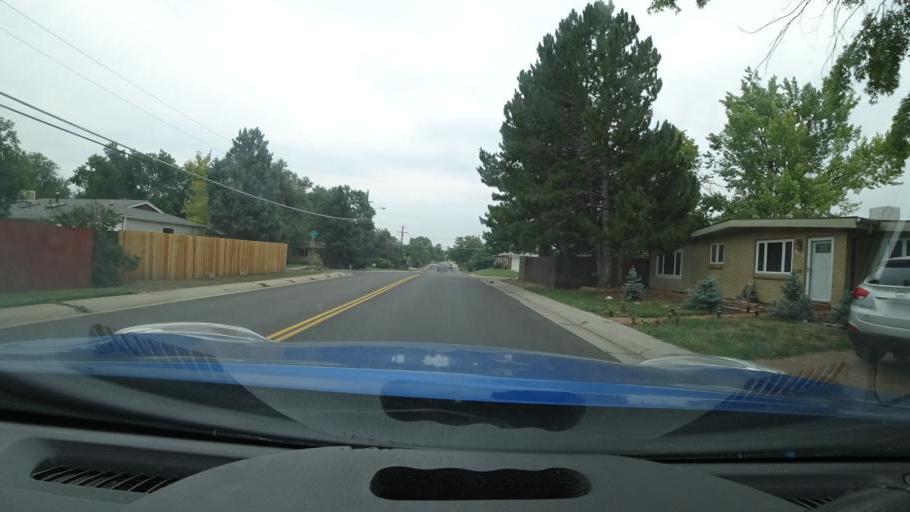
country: US
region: Colorado
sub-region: Arapahoe County
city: Glendale
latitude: 39.6894
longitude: -104.9155
